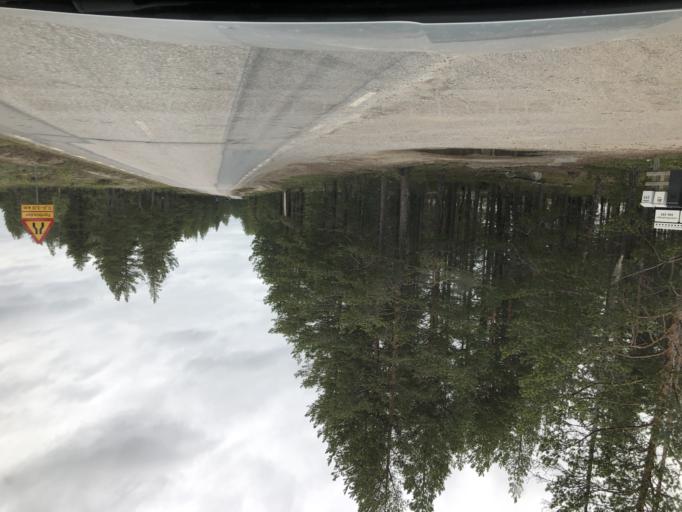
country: SE
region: Norrbotten
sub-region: Pitea Kommun
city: Pitea
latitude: 65.2405
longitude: 21.5226
